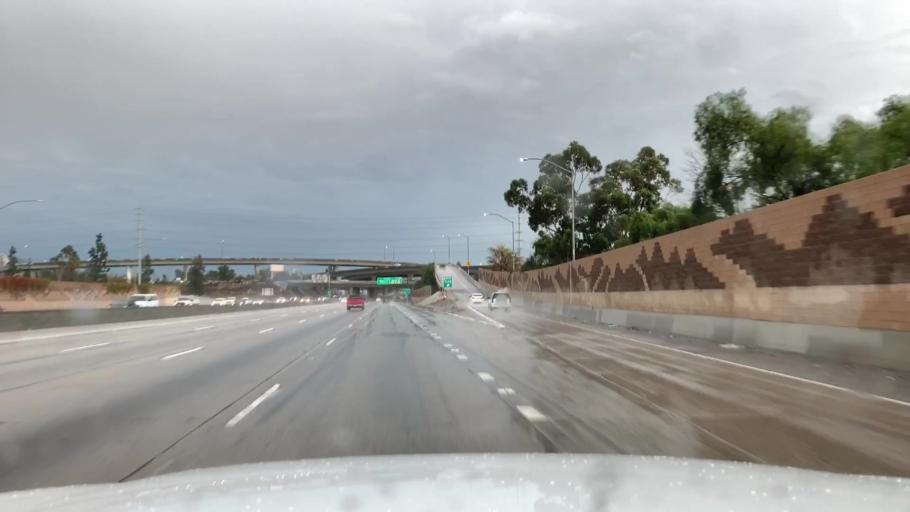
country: US
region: California
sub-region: Los Angeles County
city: San Fernando
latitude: 34.2693
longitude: -118.4464
